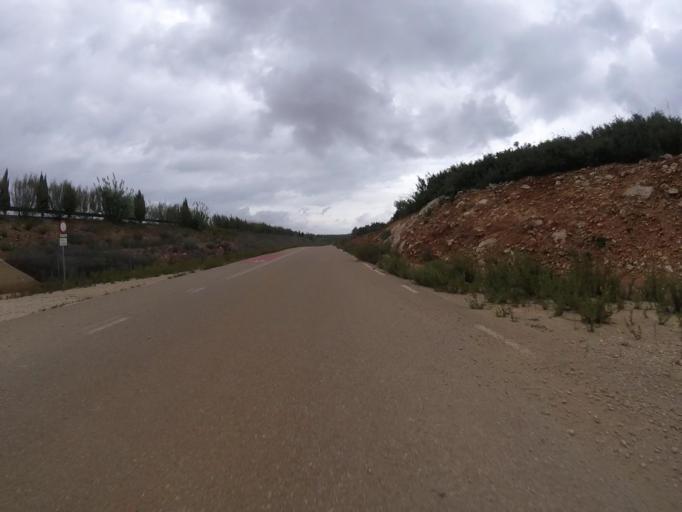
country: ES
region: Valencia
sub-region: Provincia de Castello
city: Benlloch
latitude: 40.1904
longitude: 0.0483
